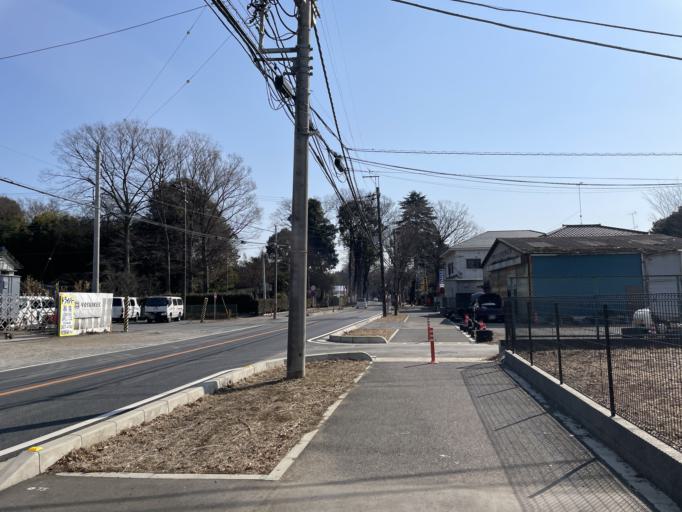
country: JP
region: Saitama
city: Oi
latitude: 35.8318
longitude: 139.5018
